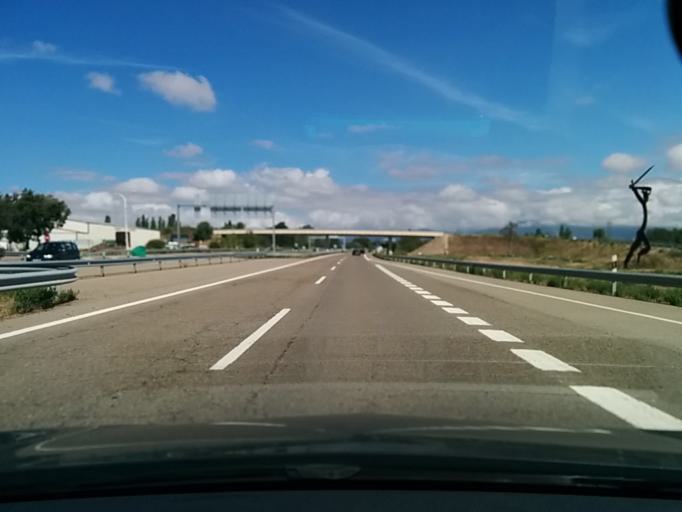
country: ES
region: Aragon
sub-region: Provincia de Huesca
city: Chimillas
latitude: 42.1626
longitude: -0.4244
